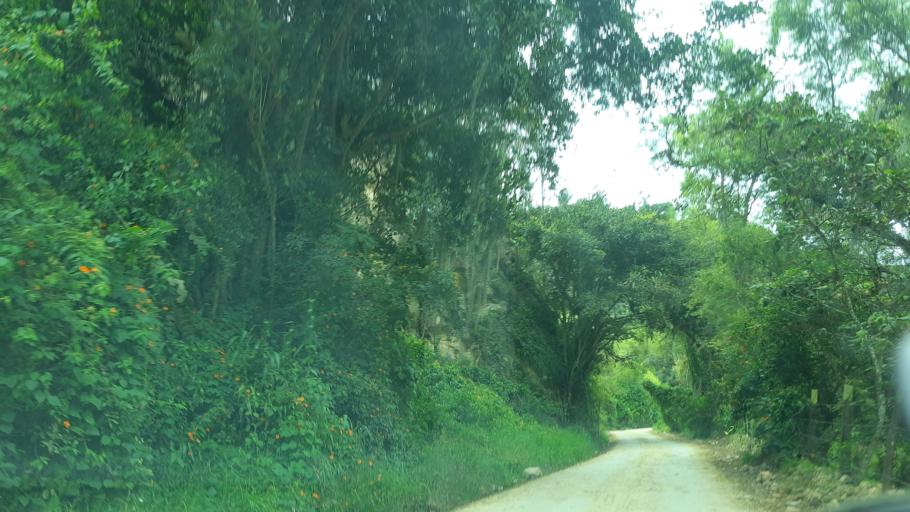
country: CO
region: Boyaca
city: Turmeque
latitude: 5.3269
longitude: -73.4479
